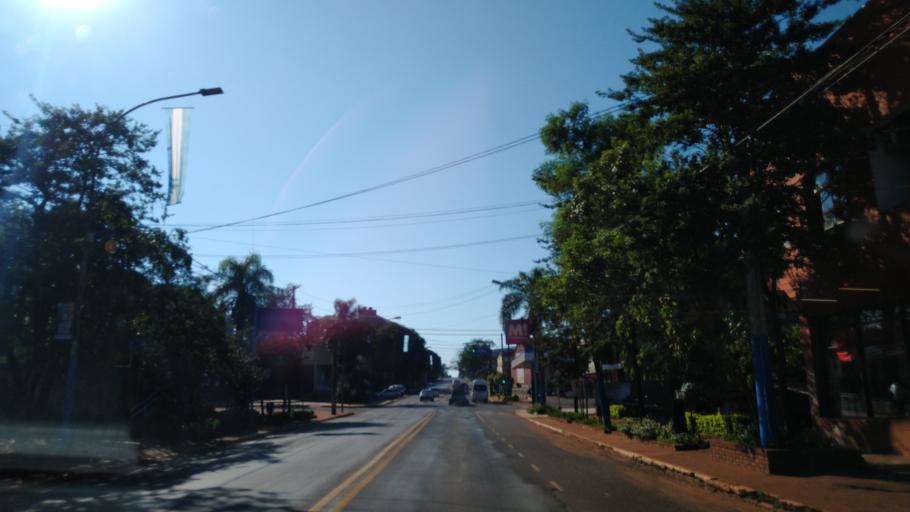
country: AR
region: Misiones
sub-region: Departamento de Montecarlo
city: Montecarlo
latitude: -26.5691
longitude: -54.7546
